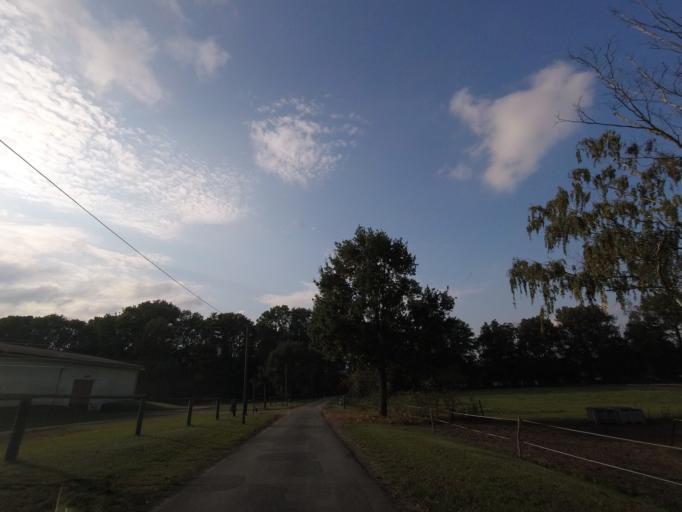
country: DE
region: Brandenburg
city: Linthe
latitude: 52.1495
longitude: 12.7231
